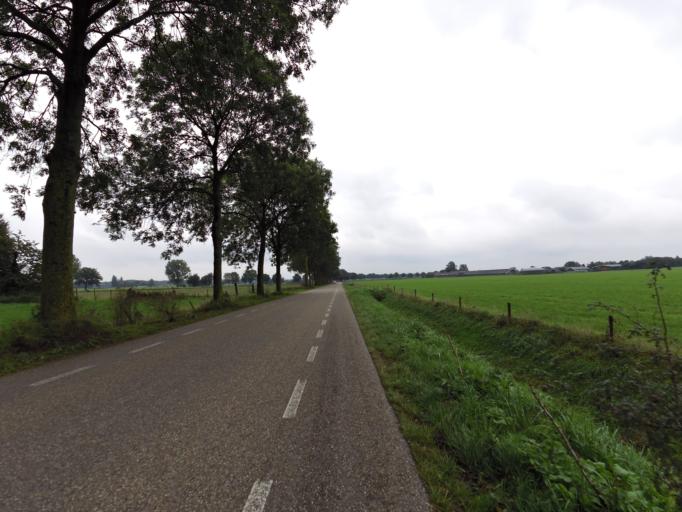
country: NL
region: Gelderland
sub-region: Gemeente Doetinchem
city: Doetinchem
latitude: 51.9344
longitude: 6.2971
